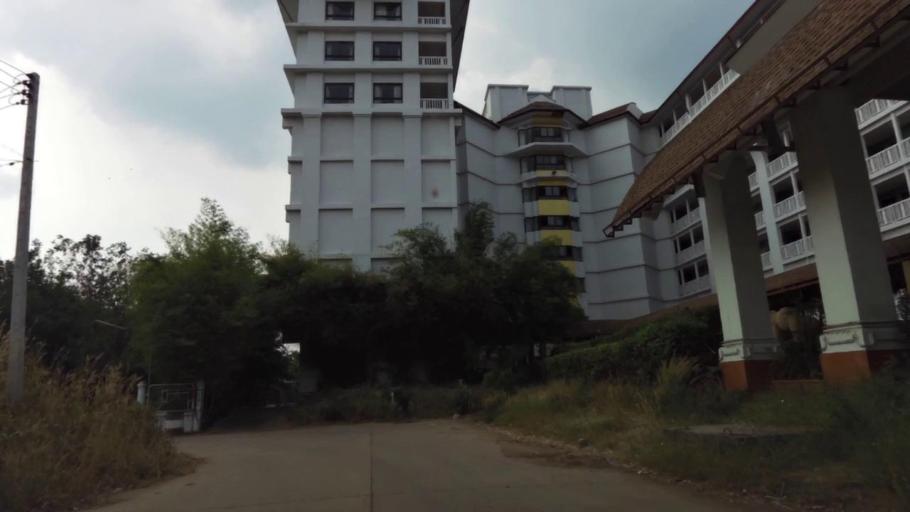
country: TH
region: Phra Nakhon Si Ayutthaya
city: Phra Nakhon Si Ayutthaya
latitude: 14.3391
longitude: 100.5792
